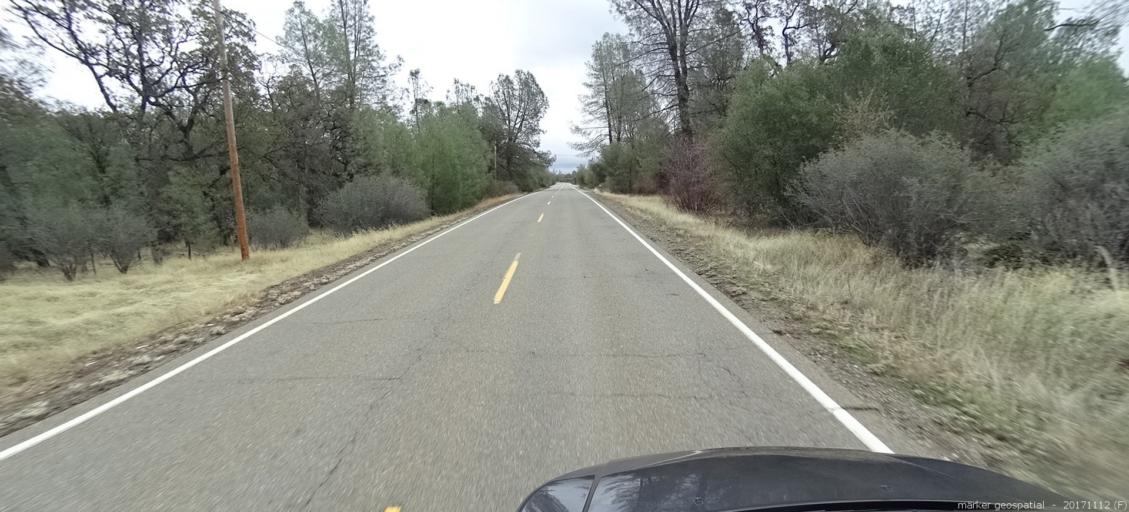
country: US
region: California
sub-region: Shasta County
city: Shingletown
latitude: 40.4896
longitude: -122.0644
